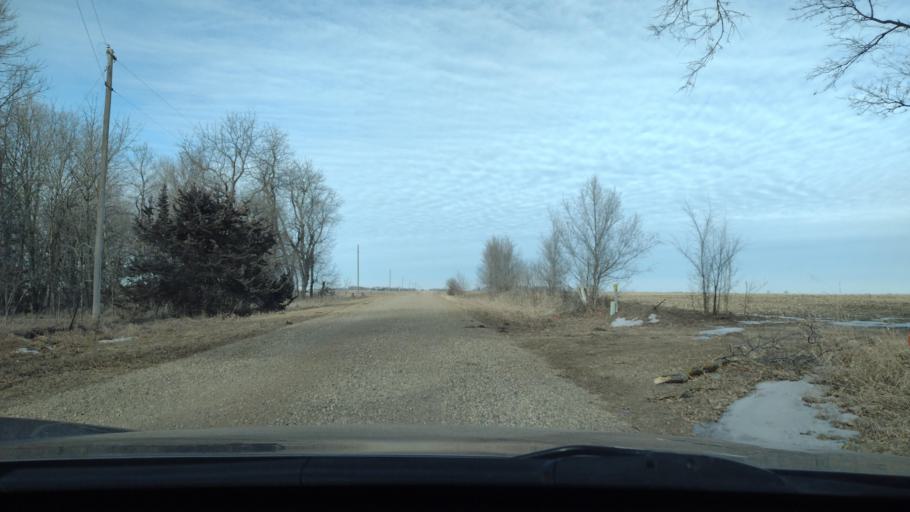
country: US
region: South Dakota
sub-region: Union County
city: Beresford
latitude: 42.9631
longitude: -96.8055
